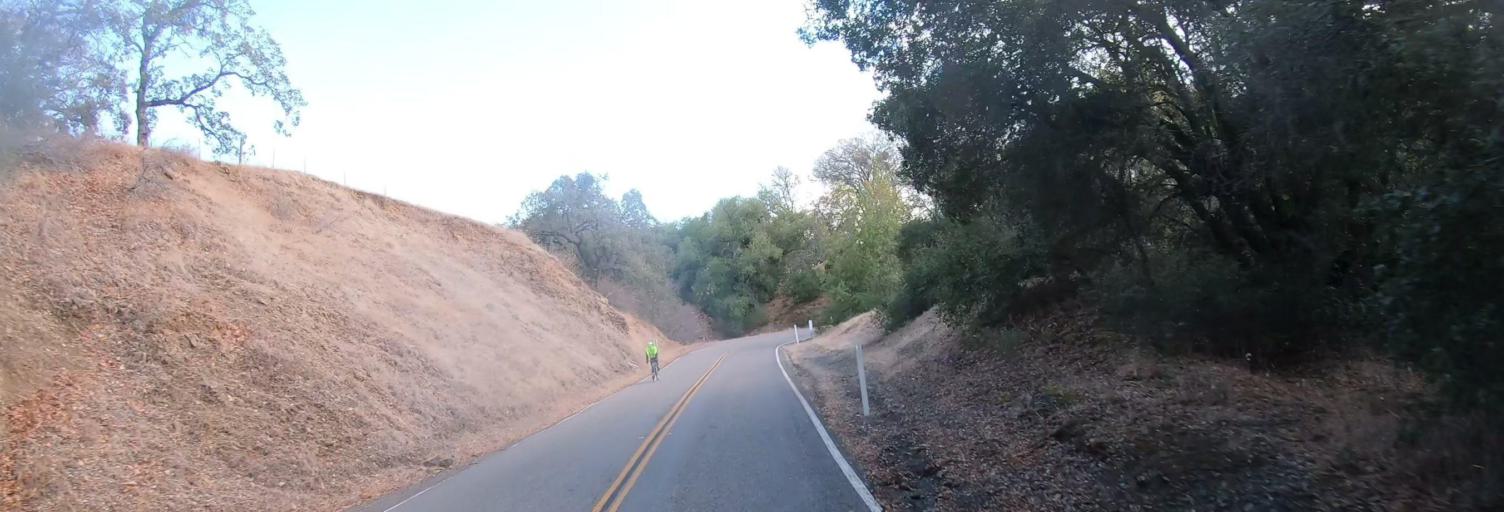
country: US
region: California
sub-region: Santa Clara County
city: East Foothills
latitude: 37.3316
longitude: -121.6856
